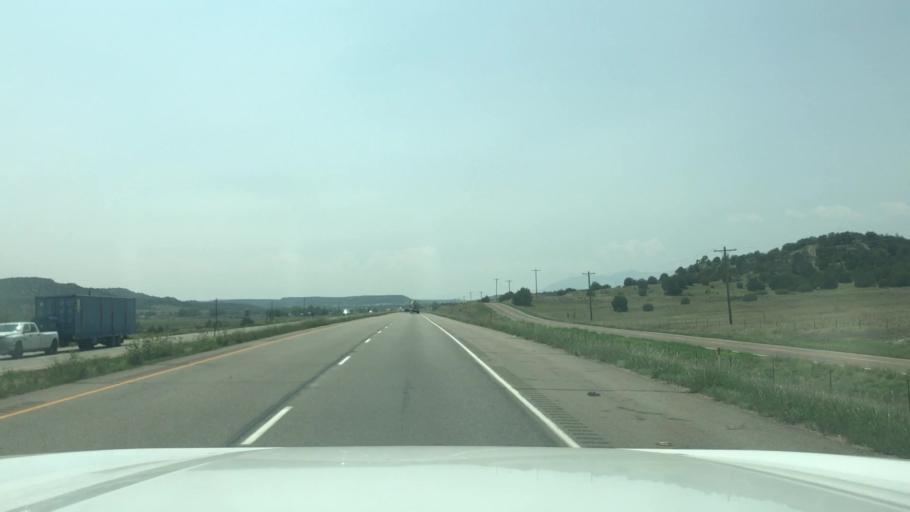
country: US
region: Colorado
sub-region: Pueblo County
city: Colorado City
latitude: 38.0186
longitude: -104.7406
